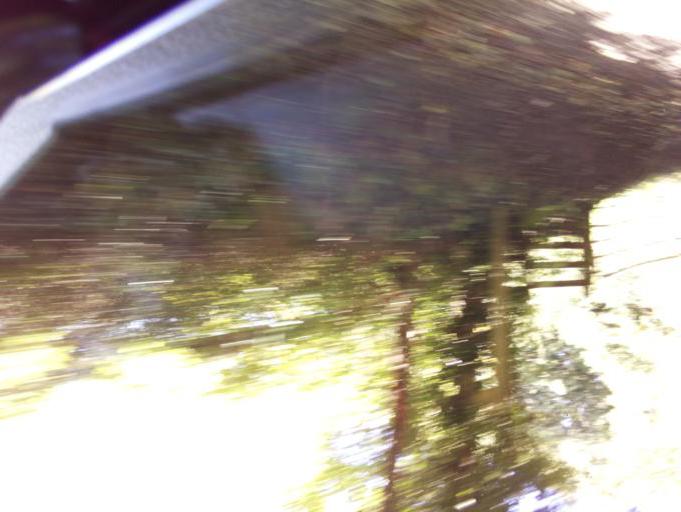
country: GB
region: Wales
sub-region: Torfaen County Borough
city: Cwmbran
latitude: 51.6214
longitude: -3.0340
